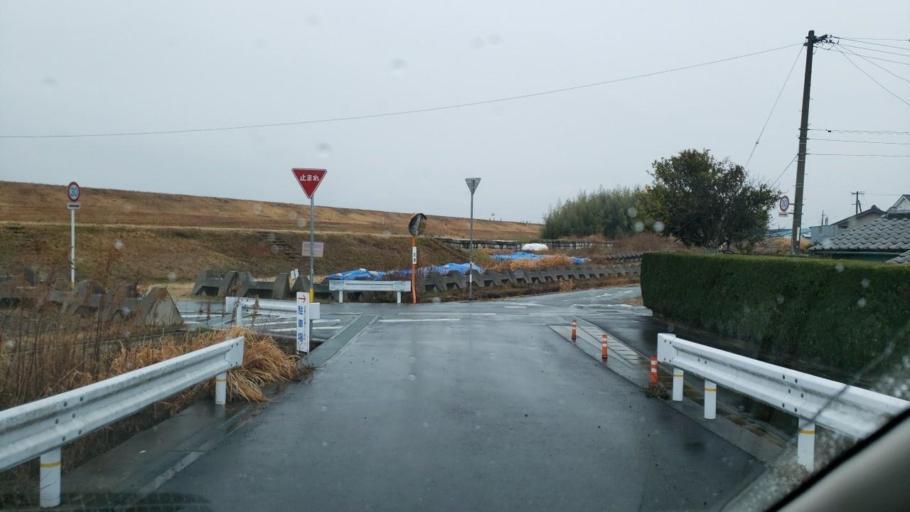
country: JP
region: Tokushima
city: Kamojimacho-jogejima
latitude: 34.0759
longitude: 134.3391
